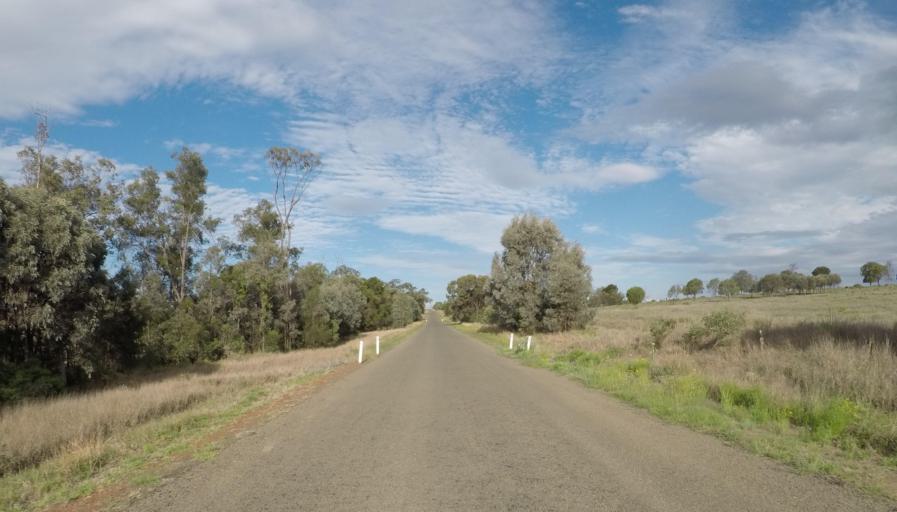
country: AU
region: Queensland
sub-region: Maranoa
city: Roma
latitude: -25.7966
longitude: 148.5003
